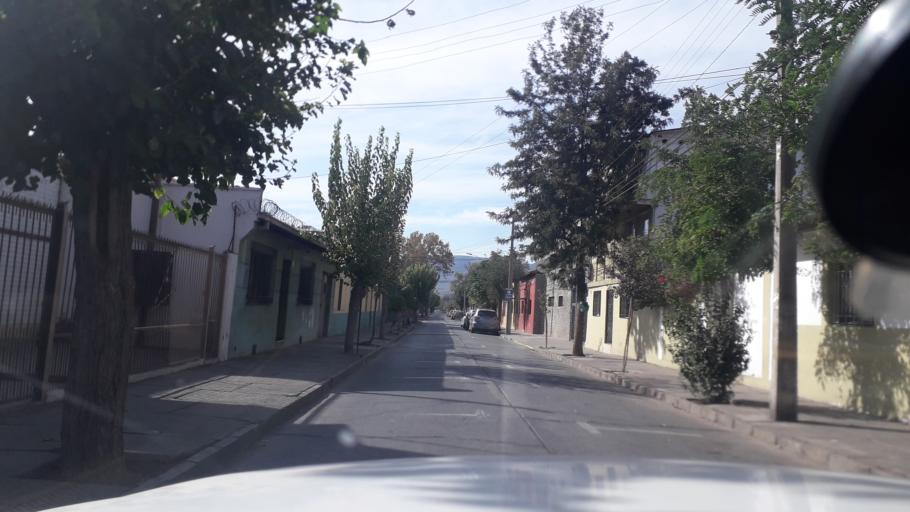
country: CL
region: Valparaiso
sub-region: Provincia de San Felipe
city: San Felipe
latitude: -32.7479
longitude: -70.7277
